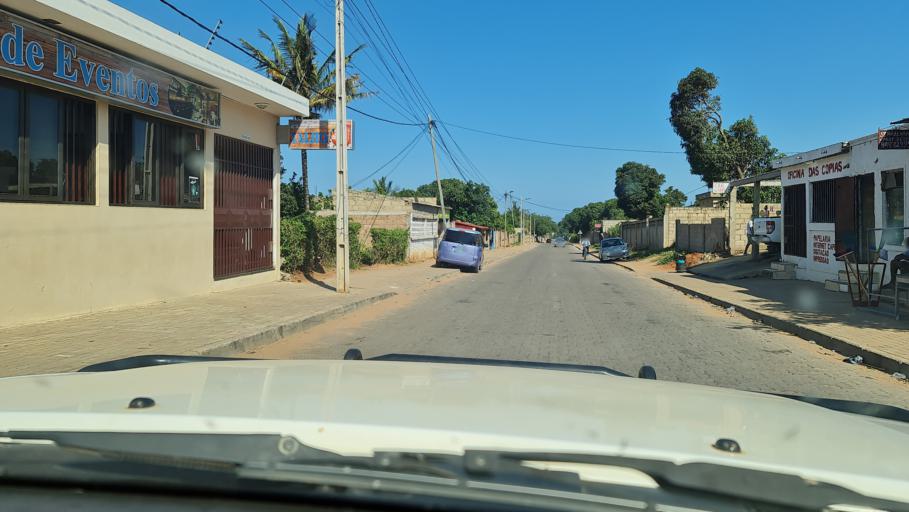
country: MZ
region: Maputo City
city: Maputo
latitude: -25.8406
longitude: 32.6377
